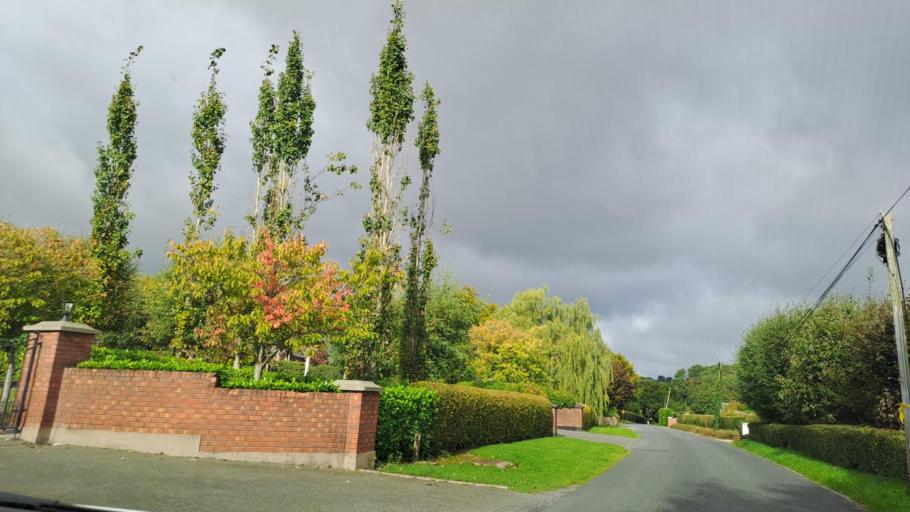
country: IE
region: Ulster
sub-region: County Monaghan
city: Carrickmacross
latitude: 53.9806
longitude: -6.7551
